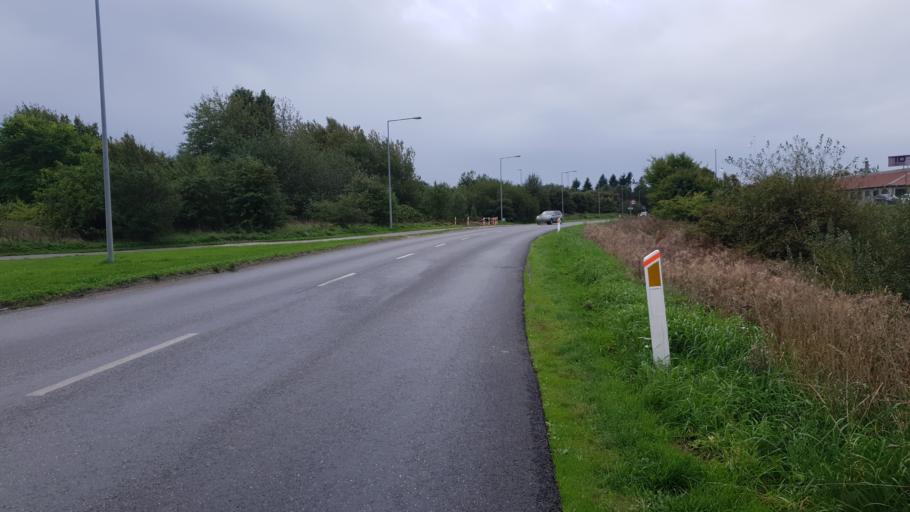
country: DK
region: Central Jutland
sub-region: Arhus Kommune
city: Tranbjerg
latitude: 56.1033
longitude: 10.1125
